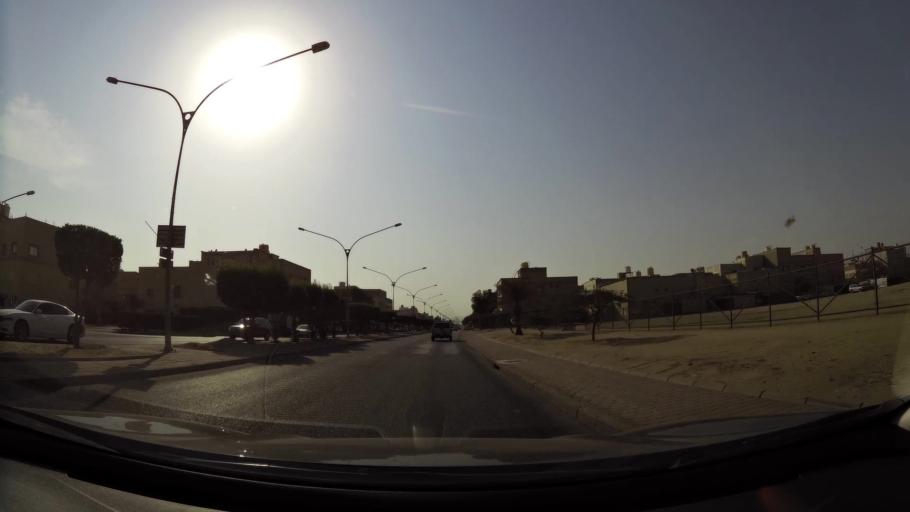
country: KW
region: Al Ahmadi
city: Ar Riqqah
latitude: 29.1627
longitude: 48.0672
